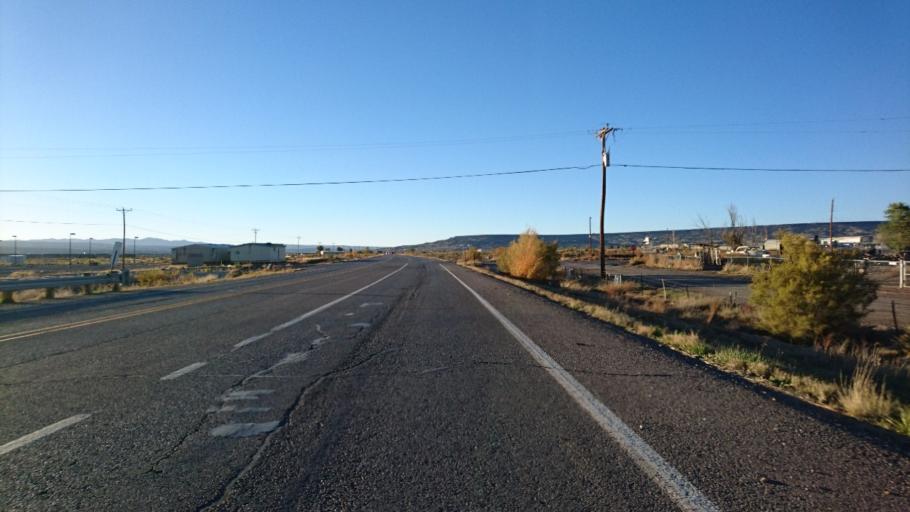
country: US
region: New Mexico
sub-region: Cibola County
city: Grants
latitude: 35.1303
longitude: -107.8100
